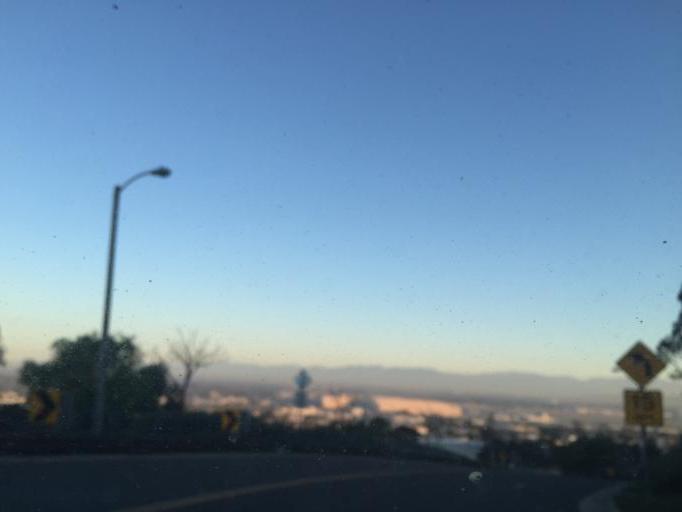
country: US
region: California
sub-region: Los Angeles County
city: Signal Hill
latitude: 33.7994
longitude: -118.1663
